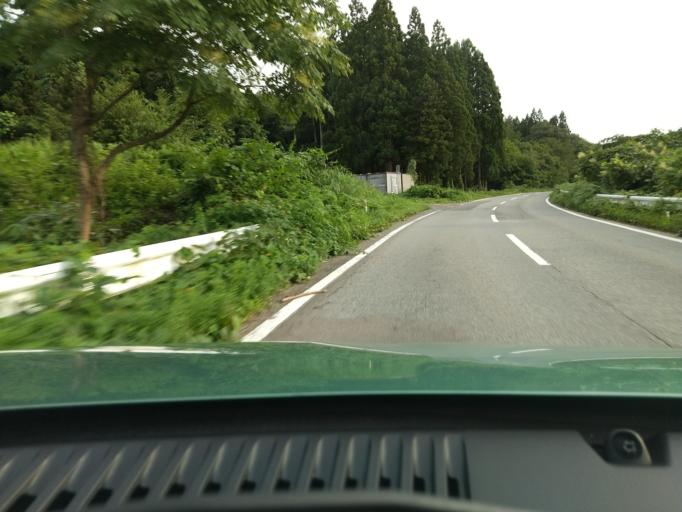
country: JP
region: Akita
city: Akita
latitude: 39.7577
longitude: 140.1609
